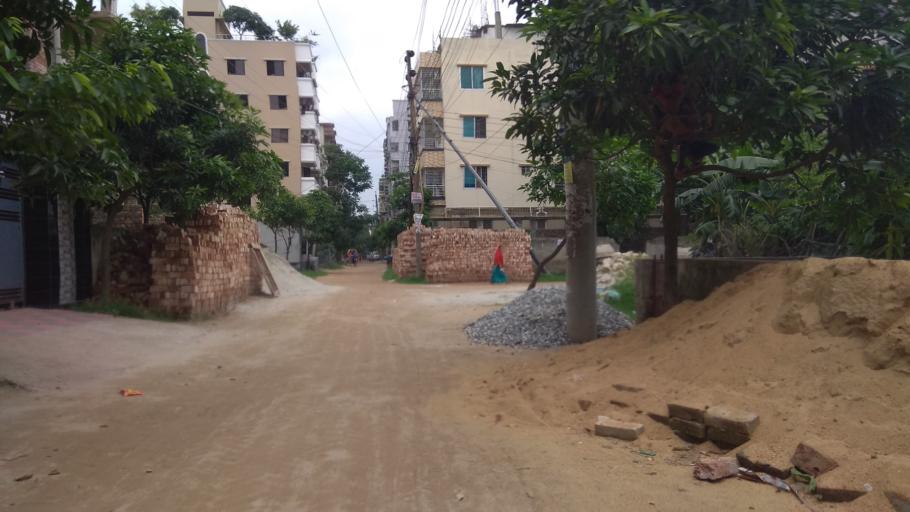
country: BD
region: Dhaka
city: Tungi
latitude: 23.8202
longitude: 90.3529
